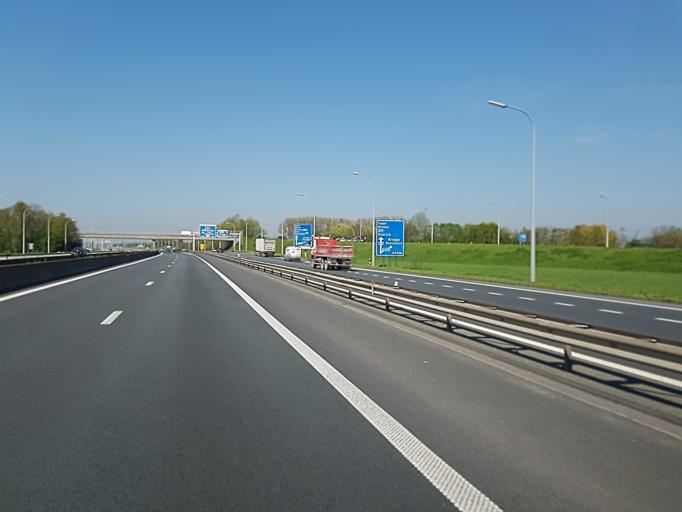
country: BE
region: Flanders
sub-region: Provincie West-Vlaanderen
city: Wevelgem
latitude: 50.8290
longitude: 3.2005
